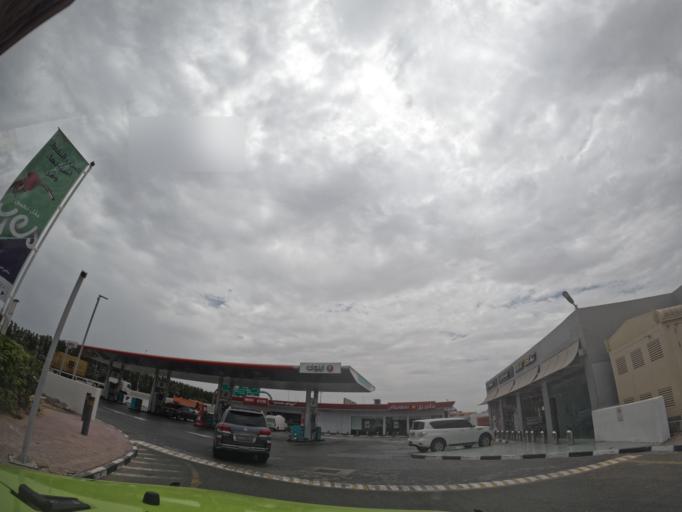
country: AE
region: Ash Shariqah
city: Sharjah
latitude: 25.2196
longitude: 55.3706
